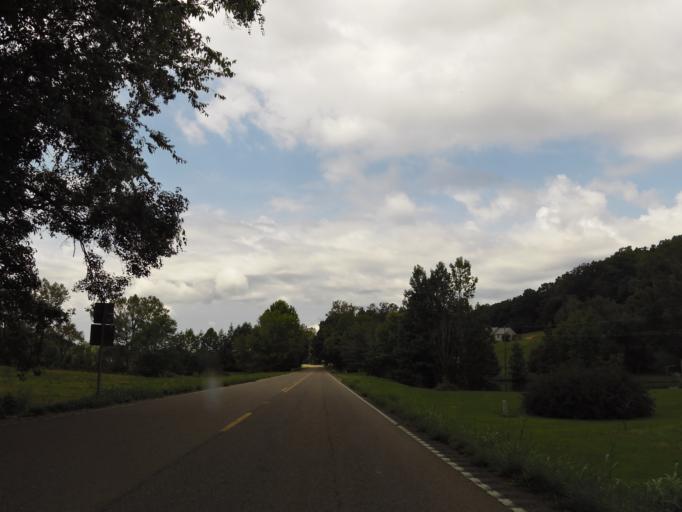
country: US
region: Tennessee
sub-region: Perry County
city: Linden
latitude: 35.6210
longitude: -87.9259
